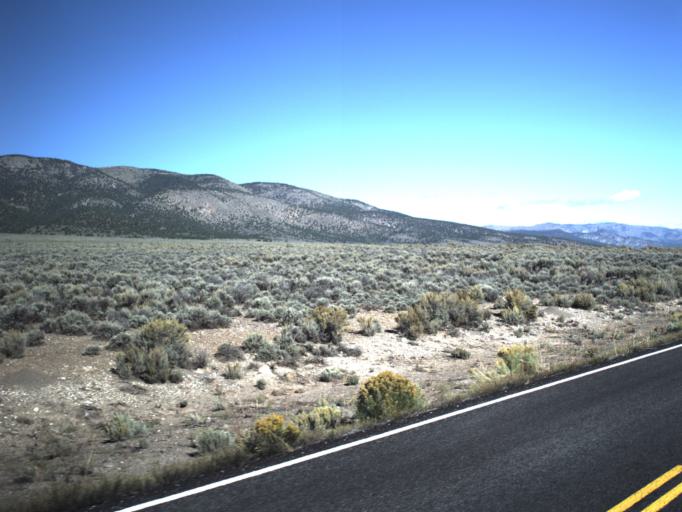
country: US
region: Utah
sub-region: Piute County
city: Junction
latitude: 38.1988
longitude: -112.0089
